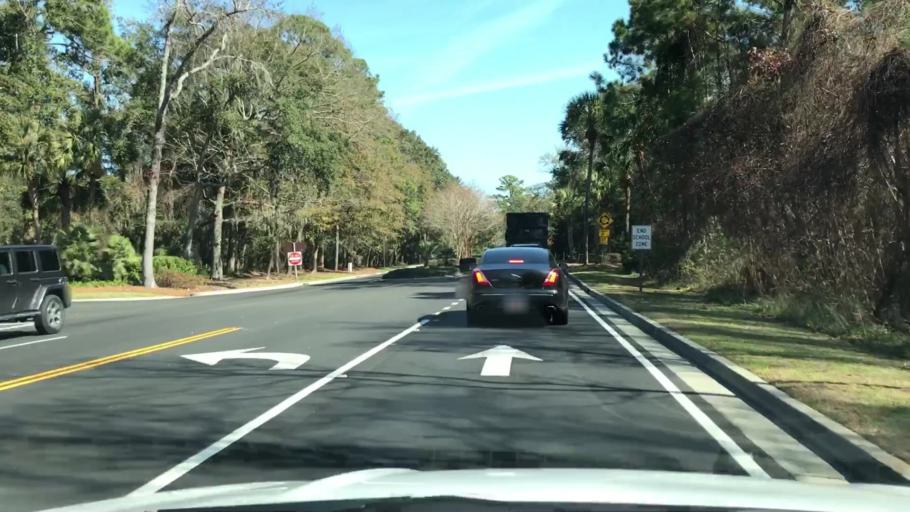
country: US
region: South Carolina
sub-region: Beaufort County
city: Hilton Head Island
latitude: 32.2218
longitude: -80.7097
